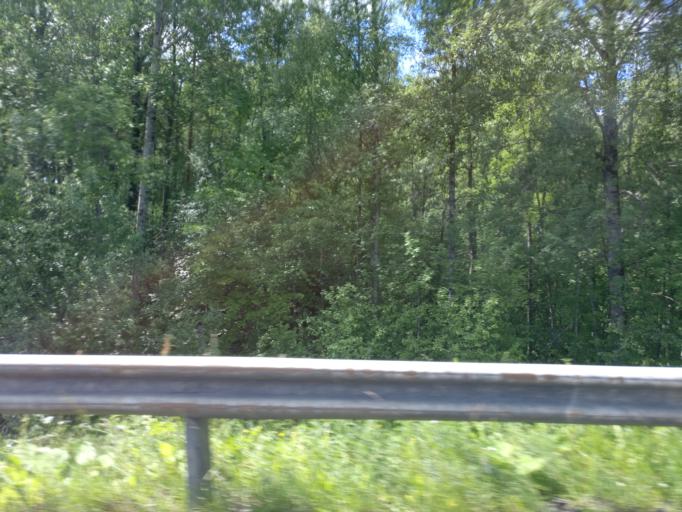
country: FI
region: Southern Savonia
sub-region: Savonlinna
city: Kerimaeki
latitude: 61.8712
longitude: 29.1241
